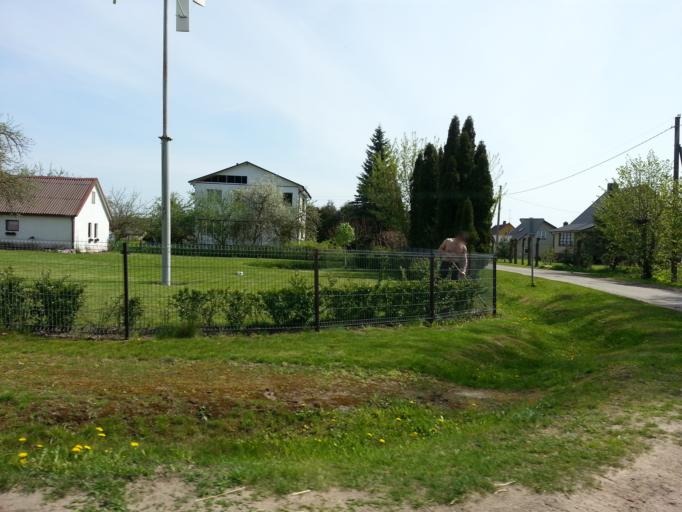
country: LT
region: Panevezys
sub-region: Panevezys City
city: Panevezys
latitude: 55.8309
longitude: 24.2547
